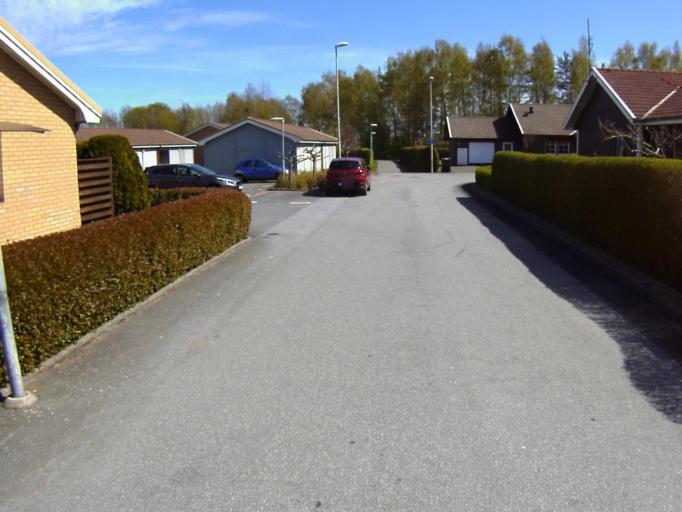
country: SE
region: Skane
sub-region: Kristianstads Kommun
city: Norra Asum
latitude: 56.0024
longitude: 14.1478
